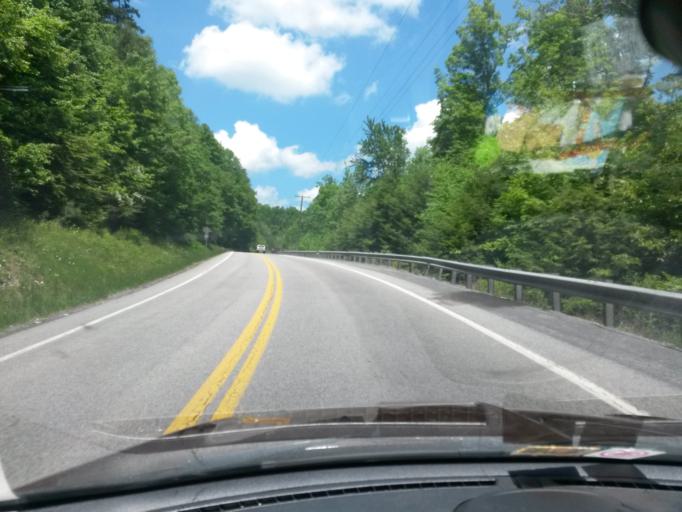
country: US
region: West Virginia
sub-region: Wyoming County
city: Pineville
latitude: 37.5978
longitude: -81.4910
